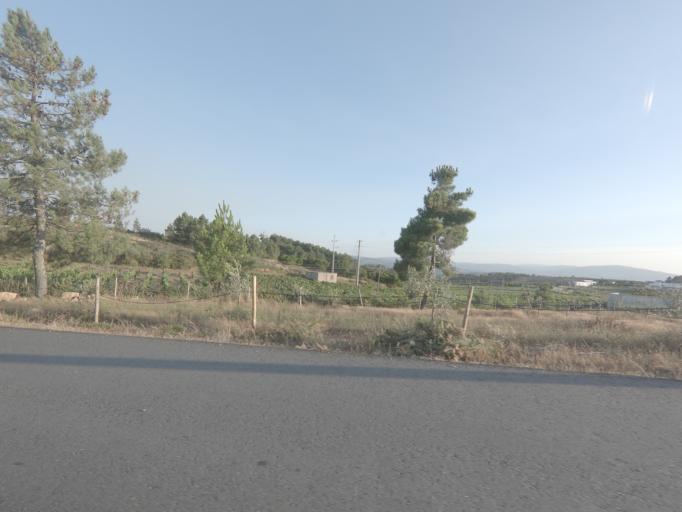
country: PT
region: Vila Real
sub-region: Sabrosa
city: Vilela
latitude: 41.2042
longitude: -7.6789
